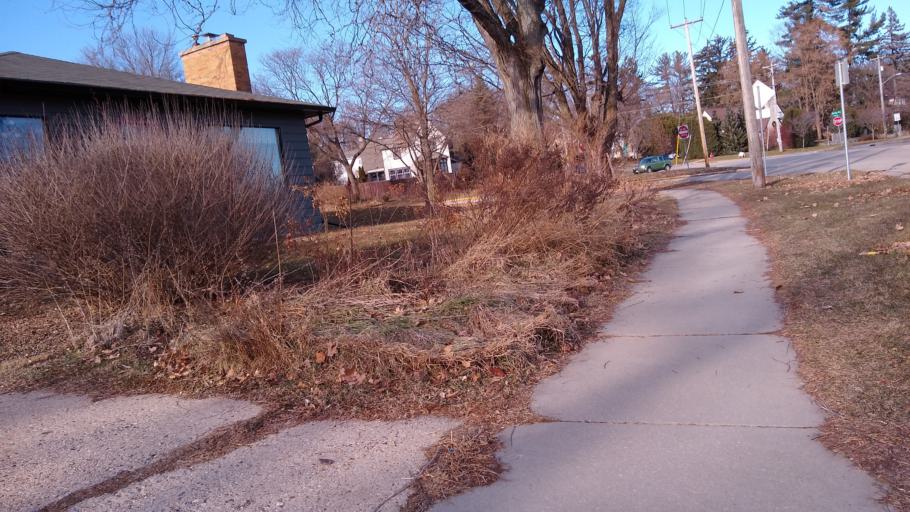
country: US
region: Wisconsin
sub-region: Dane County
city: Shorewood Hills
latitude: 43.0477
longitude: -89.4388
